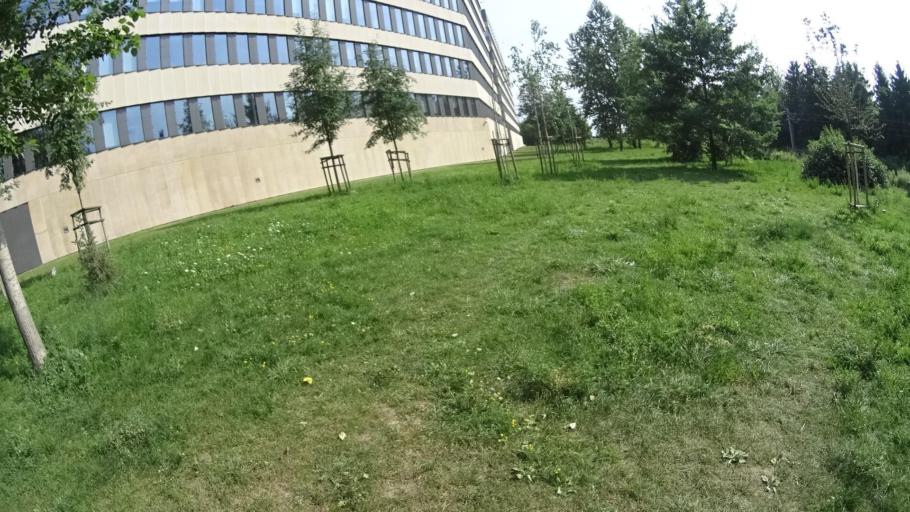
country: PL
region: Masovian Voivodeship
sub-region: Warszawa
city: Ochota
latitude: 52.1869
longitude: 20.9875
